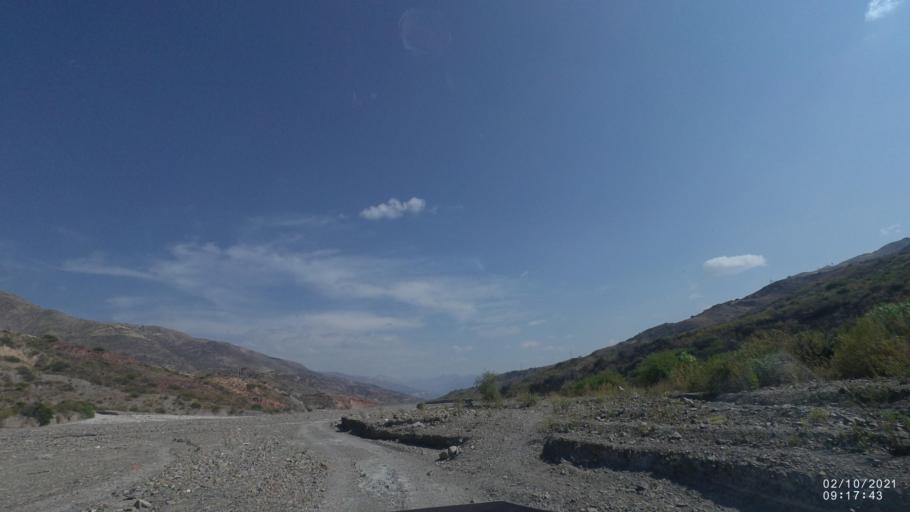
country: BO
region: Cochabamba
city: Irpa Irpa
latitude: -17.8801
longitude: -66.3054
